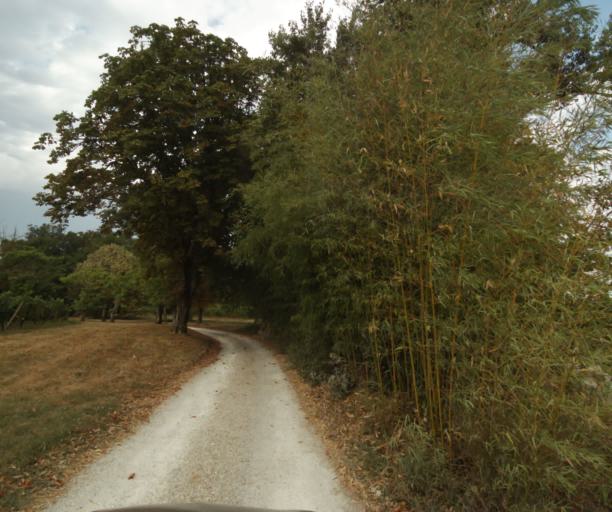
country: FR
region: Aquitaine
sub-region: Departement de la Gironde
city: Creon
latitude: 44.7656
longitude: -0.3418
